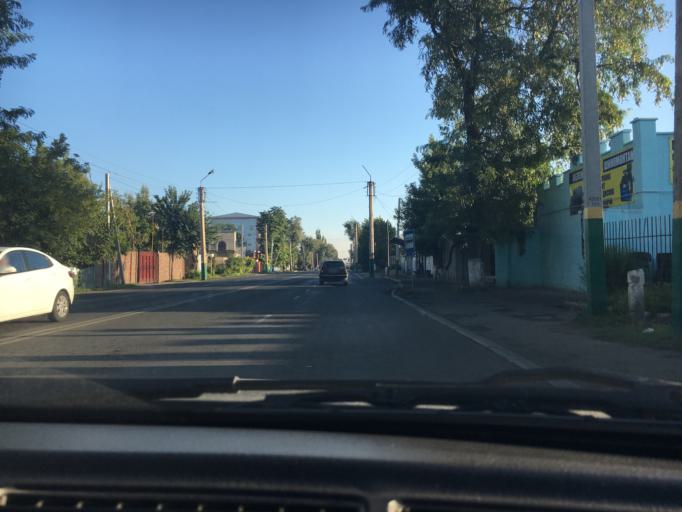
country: KZ
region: Zhambyl
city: Taraz
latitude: 42.8919
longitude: 71.3608
